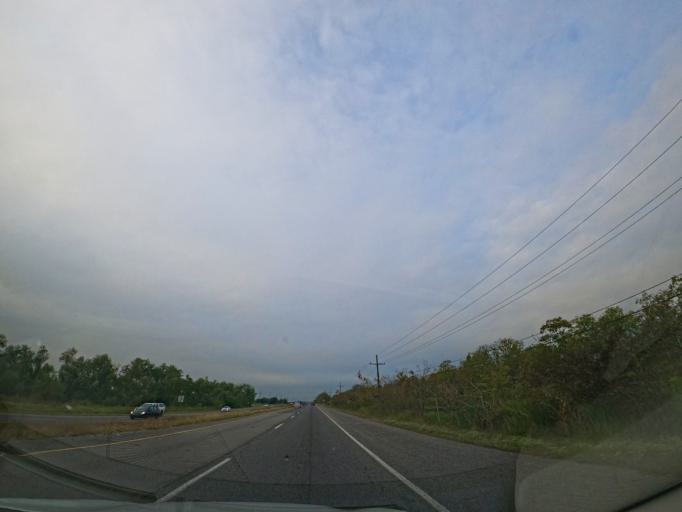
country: US
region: Louisiana
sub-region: Lafourche Parish
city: Raceland
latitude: 29.6871
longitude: -90.6425
